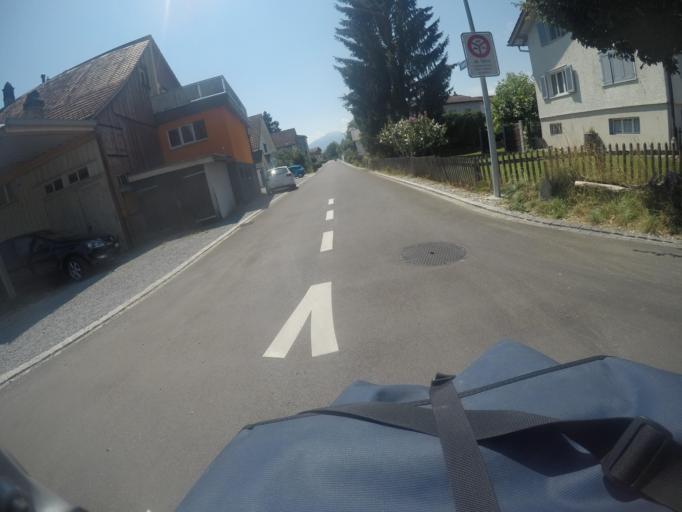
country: CH
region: Appenzell Innerrhoden
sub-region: Appenzell Inner Rhodes
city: Balgach
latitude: 47.4039
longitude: 9.6063
